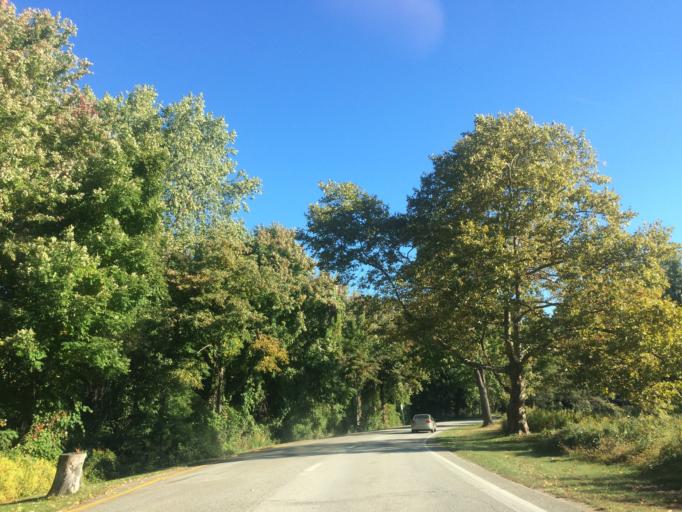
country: US
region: Pennsylvania
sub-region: Erie County
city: Erie
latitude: 42.1415
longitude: -80.1370
